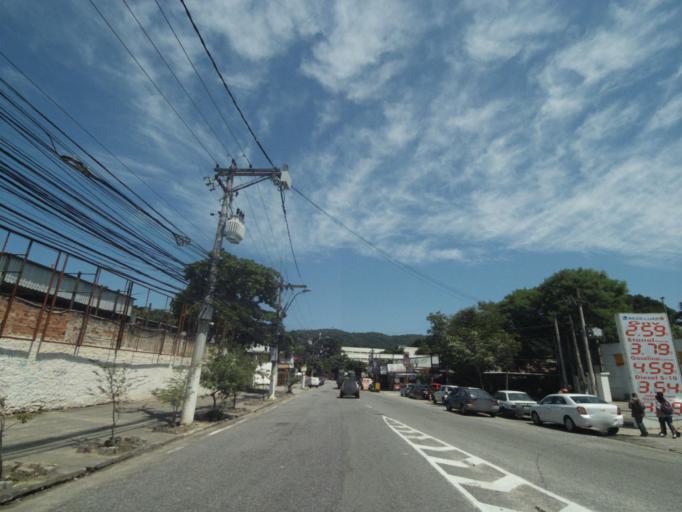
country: BR
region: Rio de Janeiro
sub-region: Niteroi
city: Niteroi
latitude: -22.9085
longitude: -43.0674
